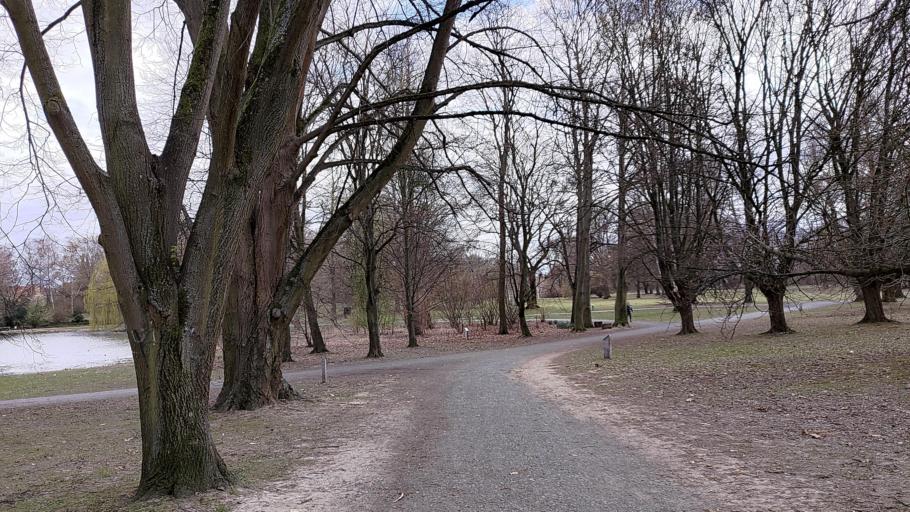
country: DE
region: Lower Saxony
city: Lengede
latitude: 52.1509
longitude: 10.3328
